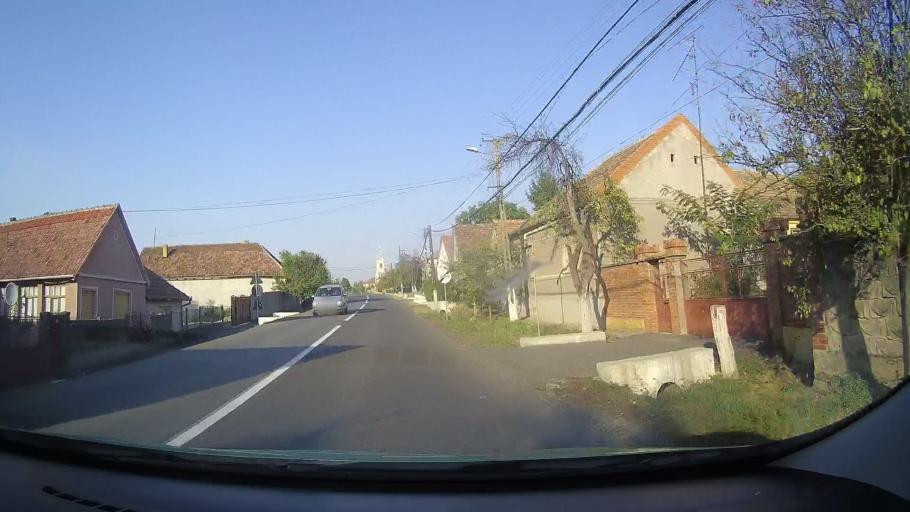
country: RO
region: Arad
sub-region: Comuna Ghioroc
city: Cuvin
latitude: 46.1638
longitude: 21.5921
